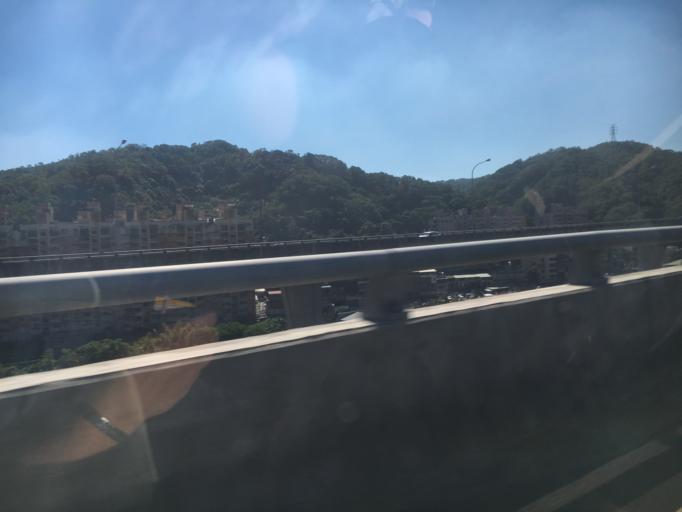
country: TW
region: Taipei
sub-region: Taipei
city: Banqiao
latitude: 25.0667
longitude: 121.4231
